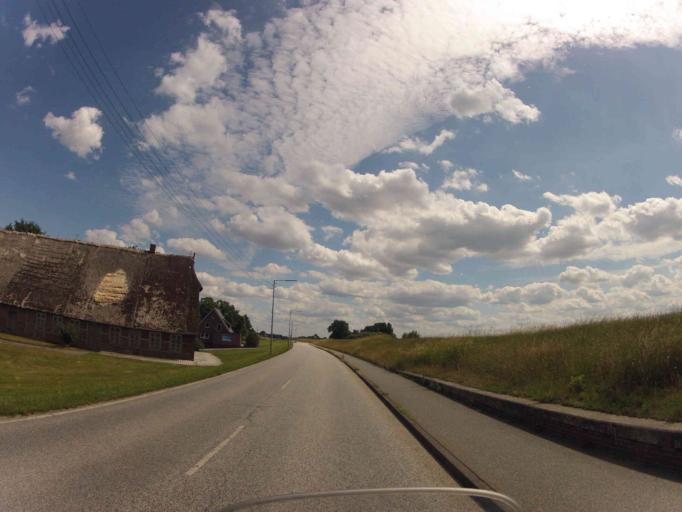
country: DE
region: Lower Saxony
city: Stelle
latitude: 53.4129
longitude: 10.1509
